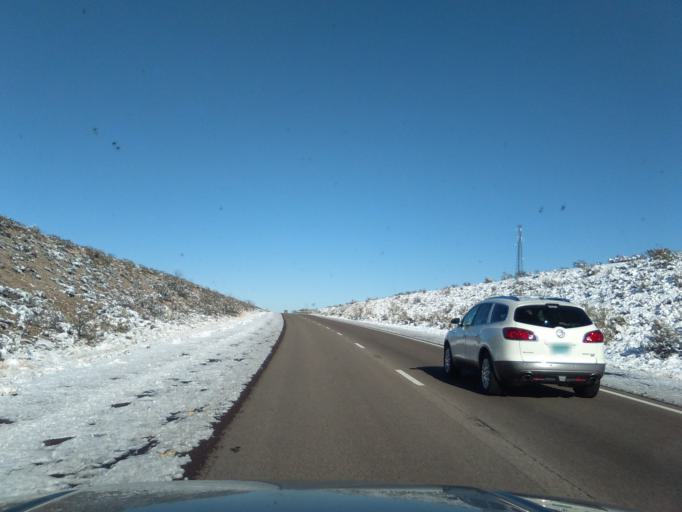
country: US
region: New Mexico
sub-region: Socorro County
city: Socorro
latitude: 33.6631
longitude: -107.0888
